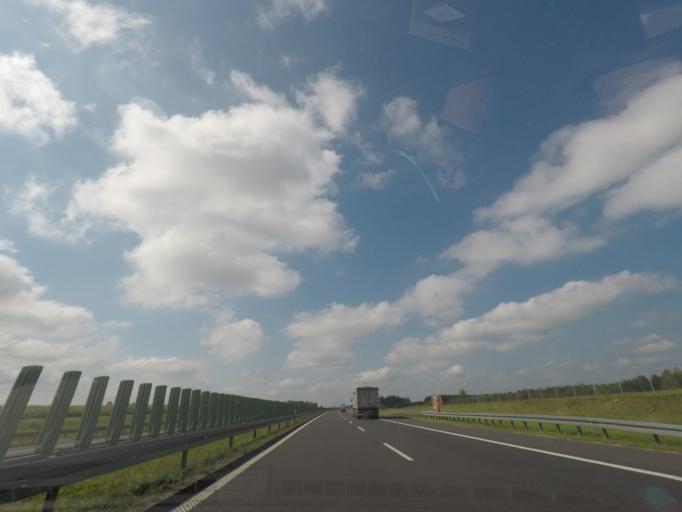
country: PL
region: Kujawsko-Pomorskie
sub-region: Powiat swiecki
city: Warlubie
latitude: 53.6139
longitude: 18.6316
